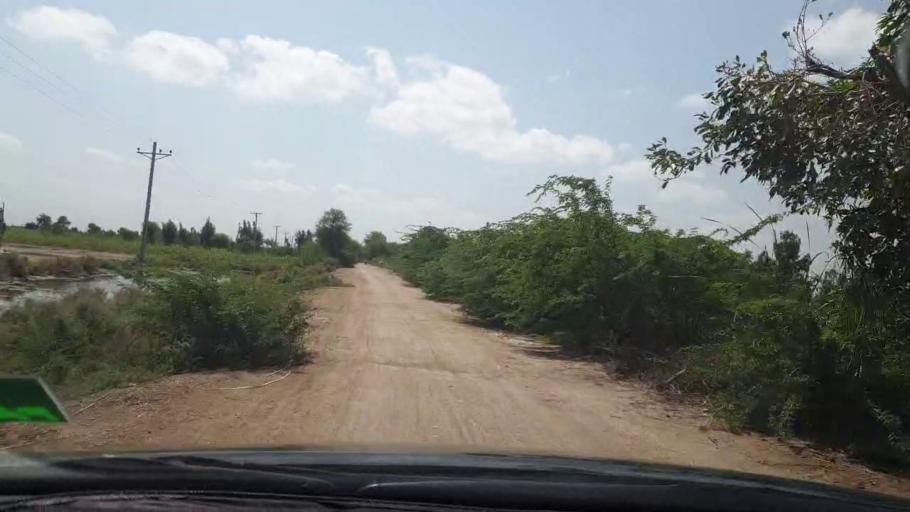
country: PK
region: Sindh
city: Tando Bago
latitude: 24.8732
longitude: 69.0859
